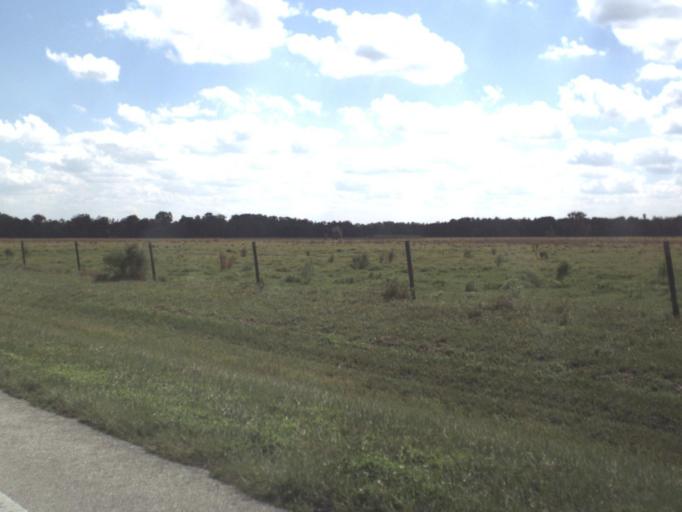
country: US
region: Florida
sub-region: Highlands County
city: Sebring
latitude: 27.4319
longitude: -81.5951
